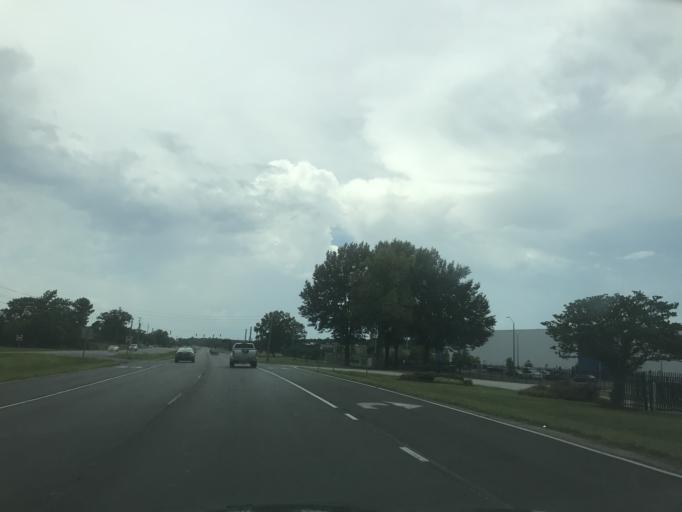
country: US
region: North Carolina
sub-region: Johnston County
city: Clayton
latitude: 35.6221
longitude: -78.4224
